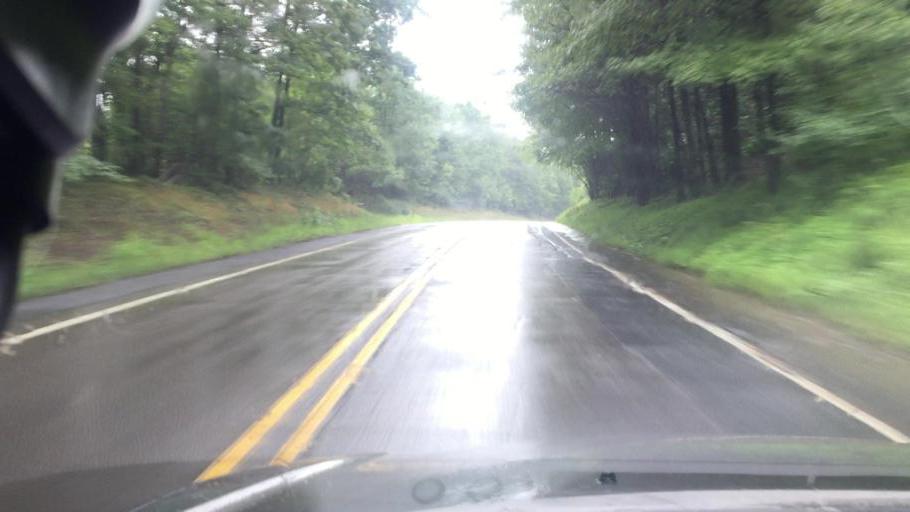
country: US
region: Pennsylvania
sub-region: Luzerne County
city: White Haven
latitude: 41.0418
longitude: -75.8324
